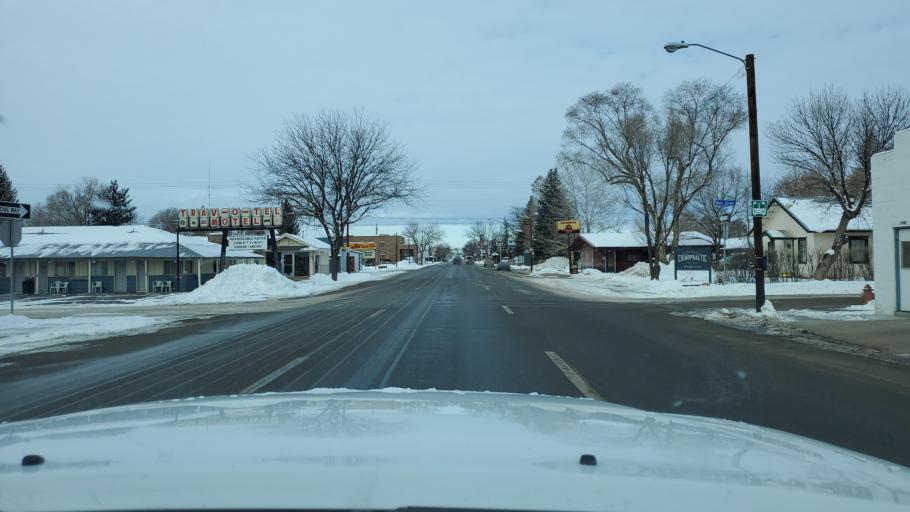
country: US
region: Colorado
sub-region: Moffat County
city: Craig
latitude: 40.5143
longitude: -107.5434
